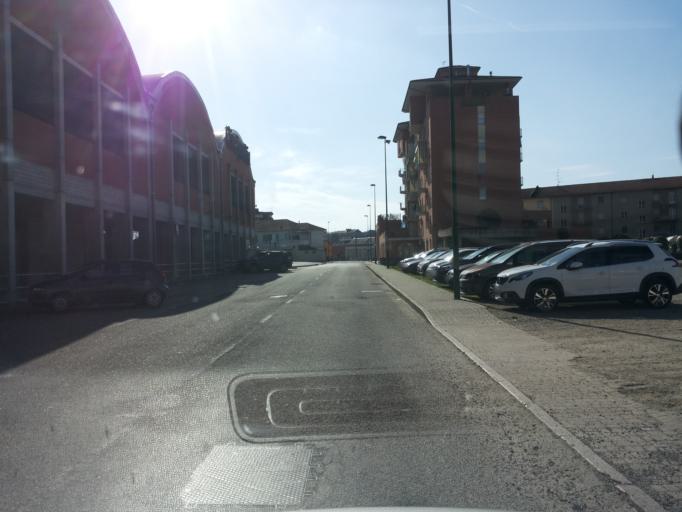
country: IT
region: Piedmont
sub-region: Provincia di Alessandria
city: Casale Monferrato
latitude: 45.1302
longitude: 8.4558
